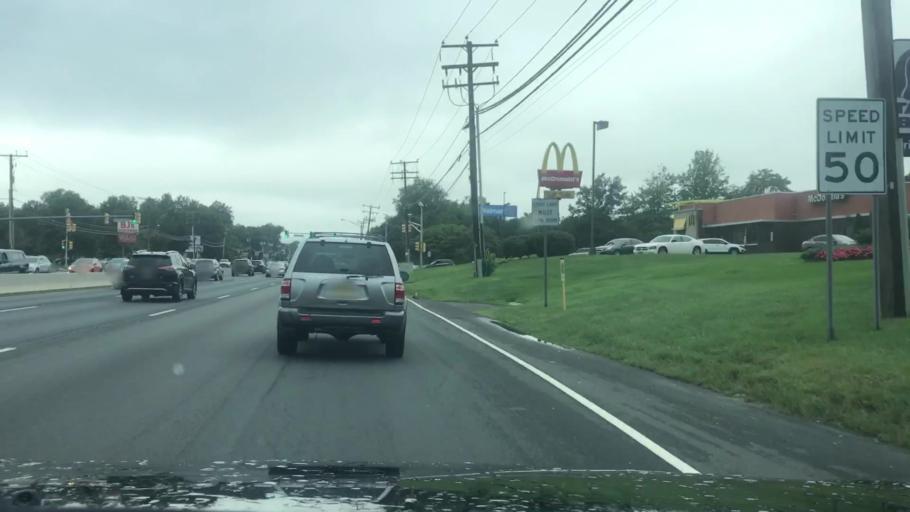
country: US
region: New Jersey
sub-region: Ocean County
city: Holiday City South
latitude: 39.9735
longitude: -74.2395
